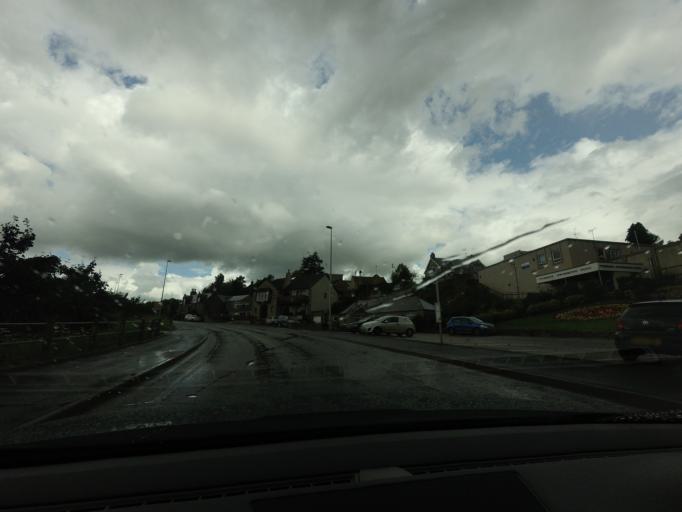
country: GB
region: Scotland
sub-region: Aberdeenshire
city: Turriff
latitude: 57.5351
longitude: -2.4617
